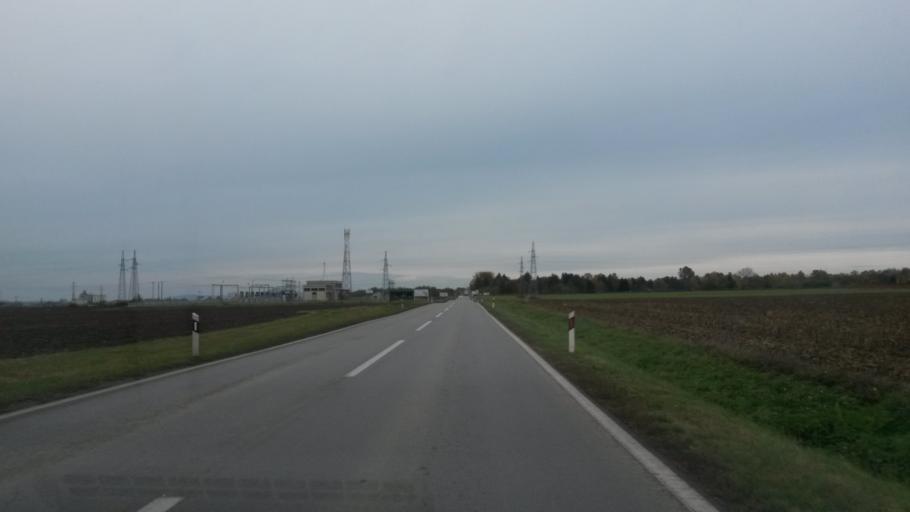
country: HR
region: Osjecko-Baranjska
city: Beli Manastir
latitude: 45.7570
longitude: 18.6317
